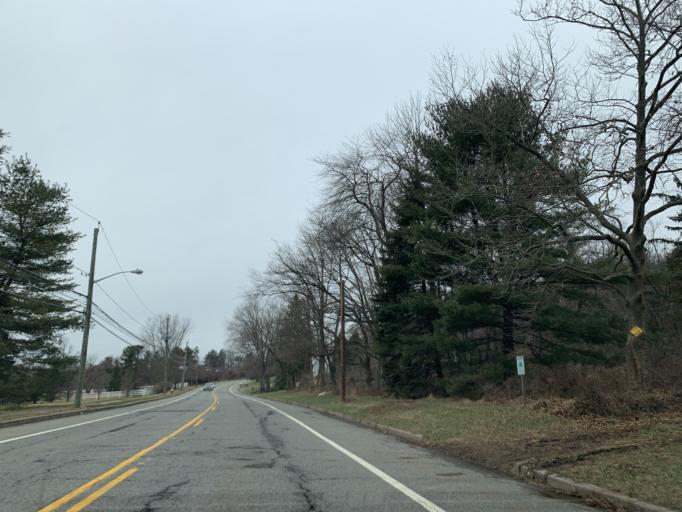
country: US
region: New Jersey
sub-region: Somerset County
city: Green Knoll
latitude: 40.6226
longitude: -74.5917
